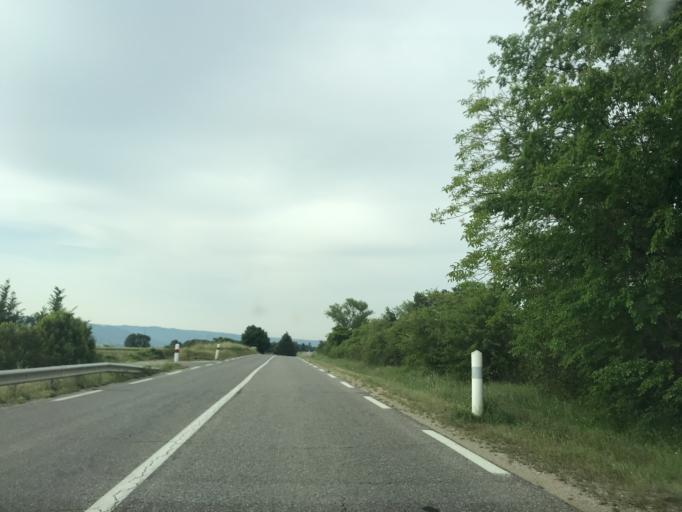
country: FR
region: Provence-Alpes-Cote d'Azur
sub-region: Departement des Alpes-de-Haute-Provence
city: Oraison
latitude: 43.9427
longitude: 5.8888
